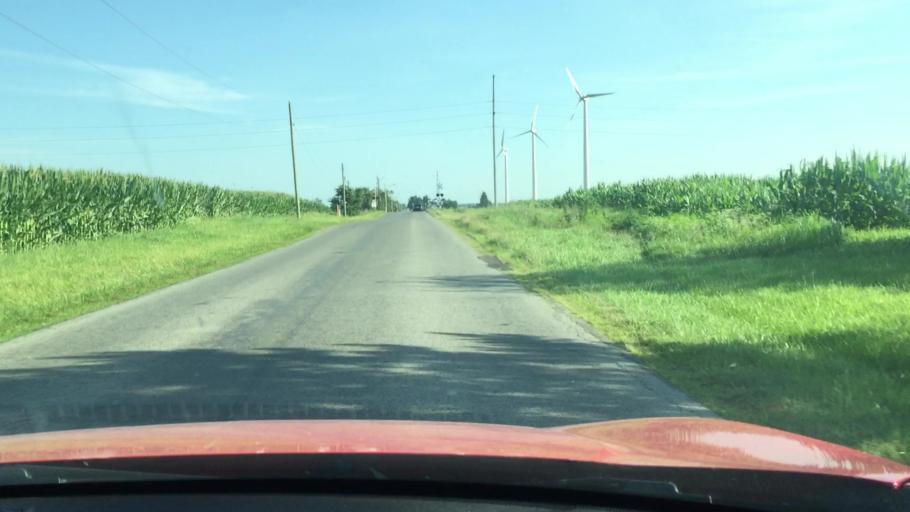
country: US
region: Ohio
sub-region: Hardin County
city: Ada
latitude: 40.7703
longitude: -83.8423
